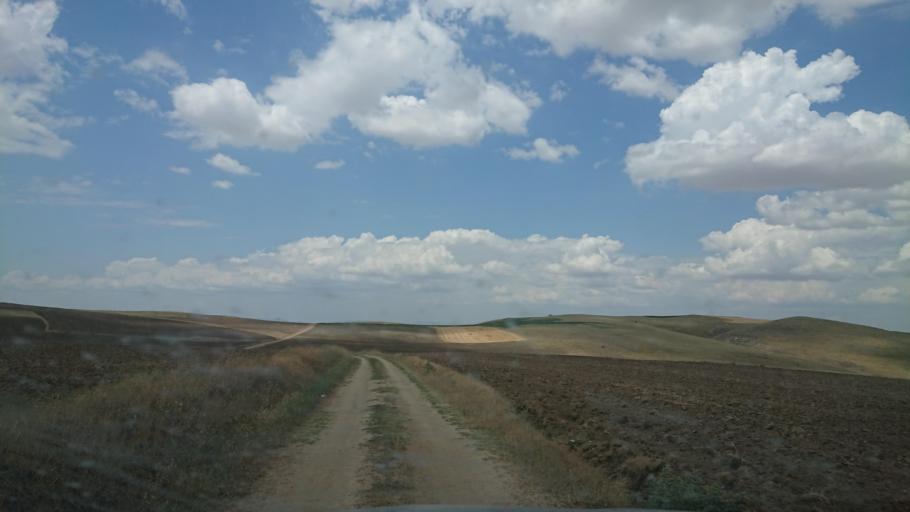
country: TR
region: Aksaray
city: Agacoren
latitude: 38.8987
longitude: 33.8830
